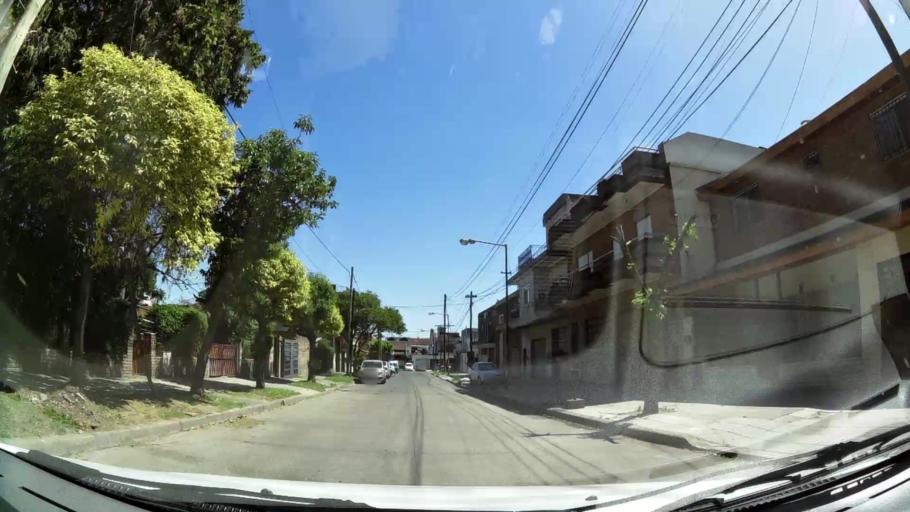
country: AR
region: Buenos Aires
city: Caseros
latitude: -34.5724
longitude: -58.5562
